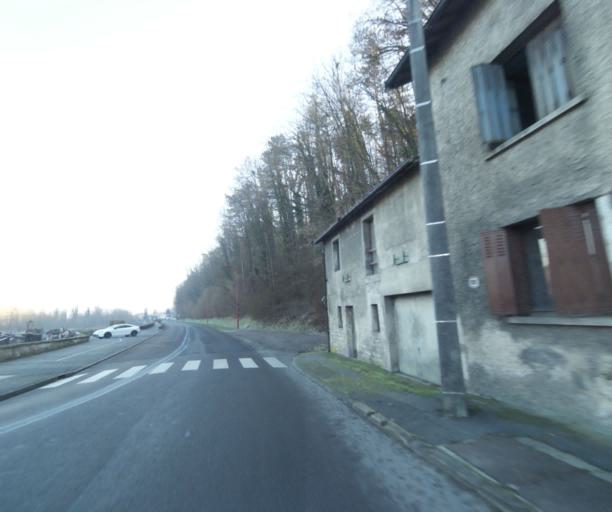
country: FR
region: Champagne-Ardenne
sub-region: Departement de la Haute-Marne
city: Bienville
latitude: 48.5477
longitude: 5.0743
